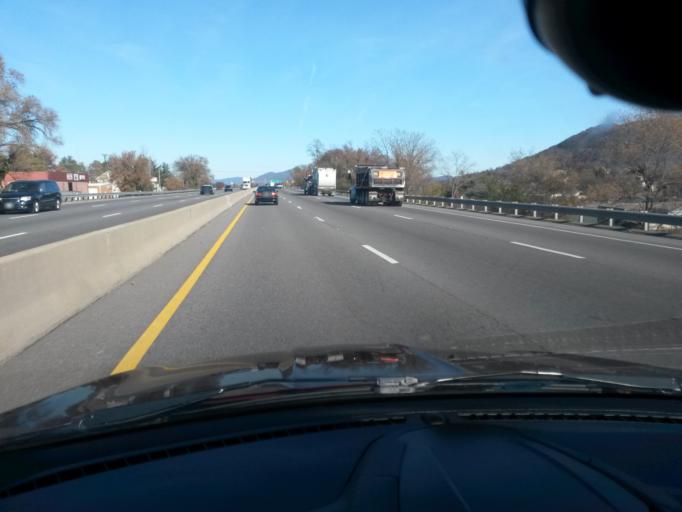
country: US
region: Virginia
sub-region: City of Roanoke
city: Roanoke
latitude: 37.2493
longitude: -79.9626
